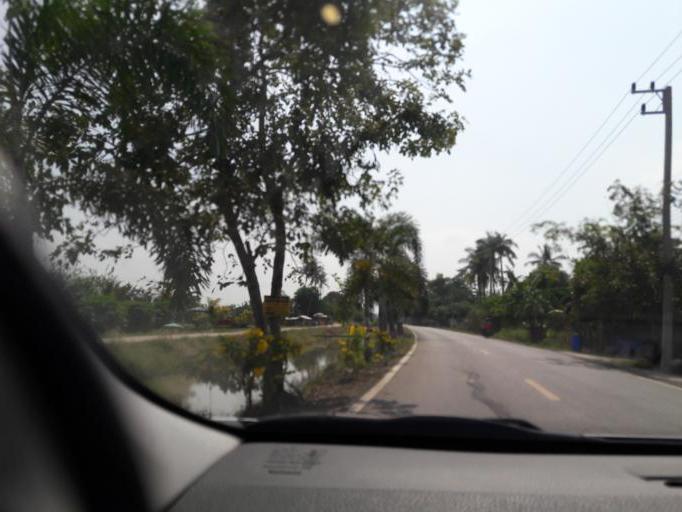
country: TH
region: Ang Thong
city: Ang Thong
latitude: 14.5828
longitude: 100.3965
